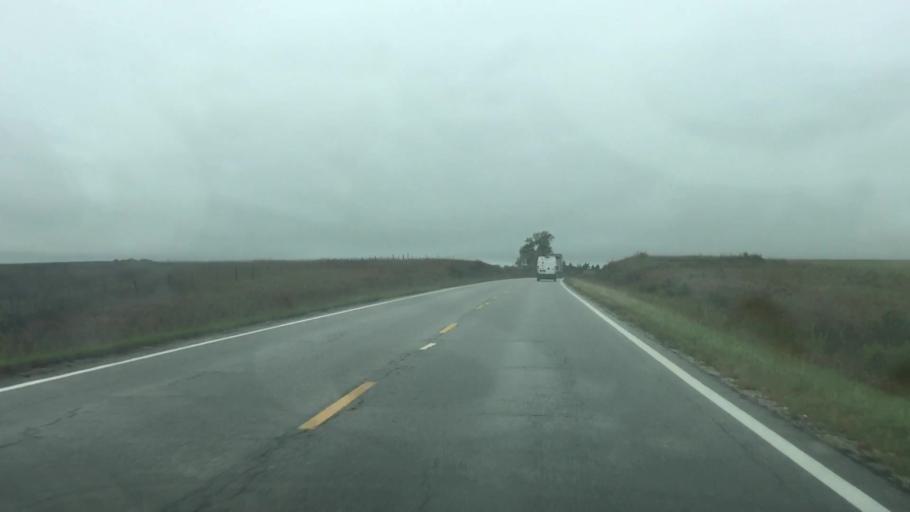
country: US
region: Kansas
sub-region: Anderson County
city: Garnett
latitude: 38.1808
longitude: -95.2645
